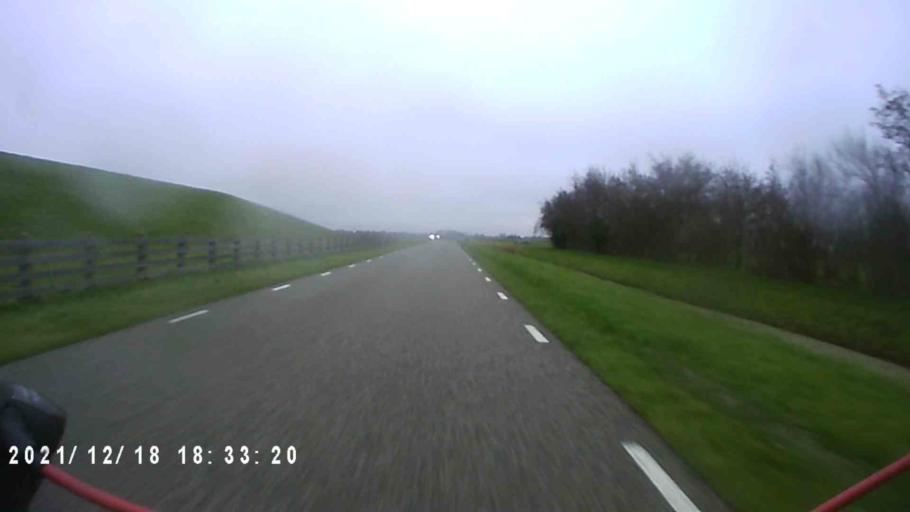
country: NL
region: Friesland
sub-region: Gemeente Dongeradeel
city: Ternaard
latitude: 53.4014
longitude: 6.0221
